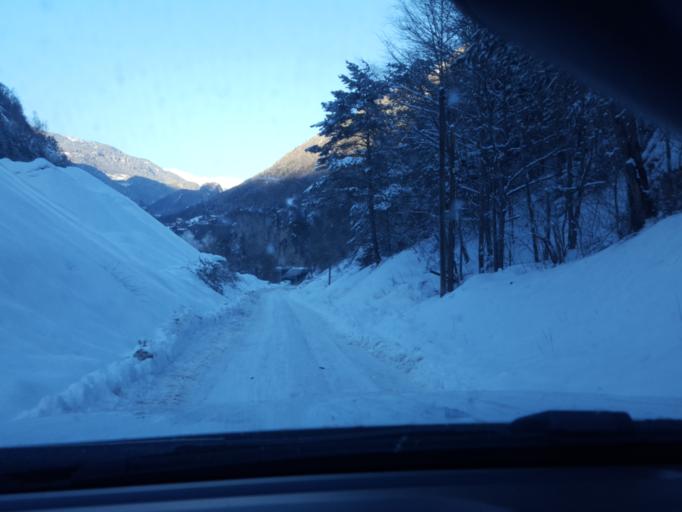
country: FR
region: Rhone-Alpes
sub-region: Departement de la Savoie
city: Salins-les-Thermes
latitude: 45.4629
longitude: 6.5239
